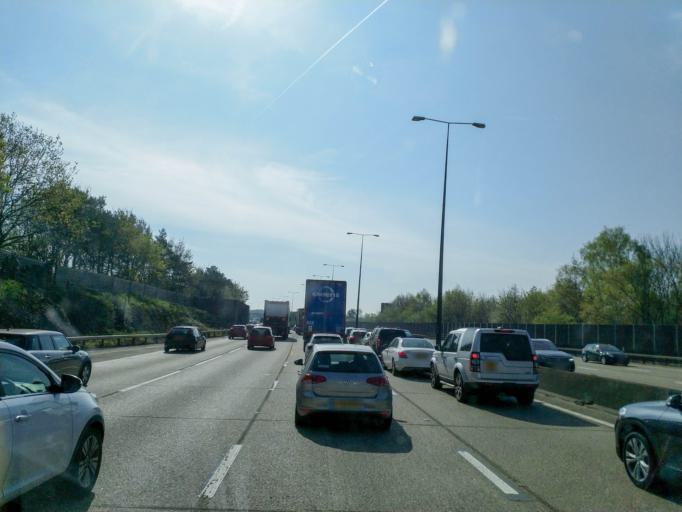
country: GB
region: England
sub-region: Surrey
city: Byfleet
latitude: 51.3297
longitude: -0.4789
